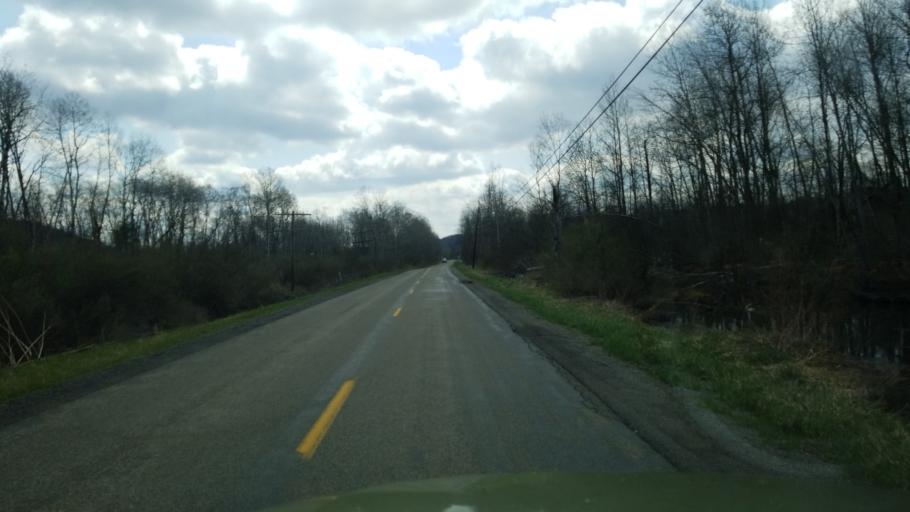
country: US
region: Pennsylvania
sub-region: Jefferson County
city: Brockway
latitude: 41.2595
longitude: -78.8069
